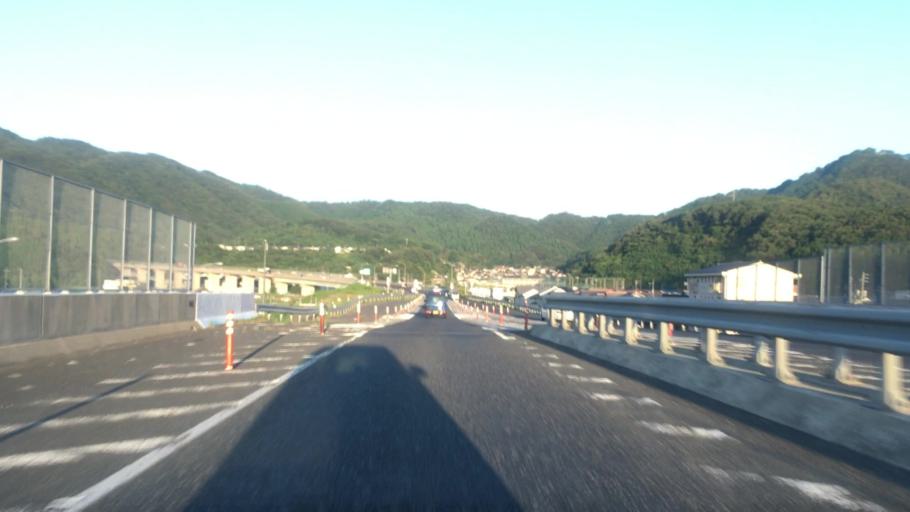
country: JP
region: Tottori
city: Tottori
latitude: 35.5228
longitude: 134.2289
